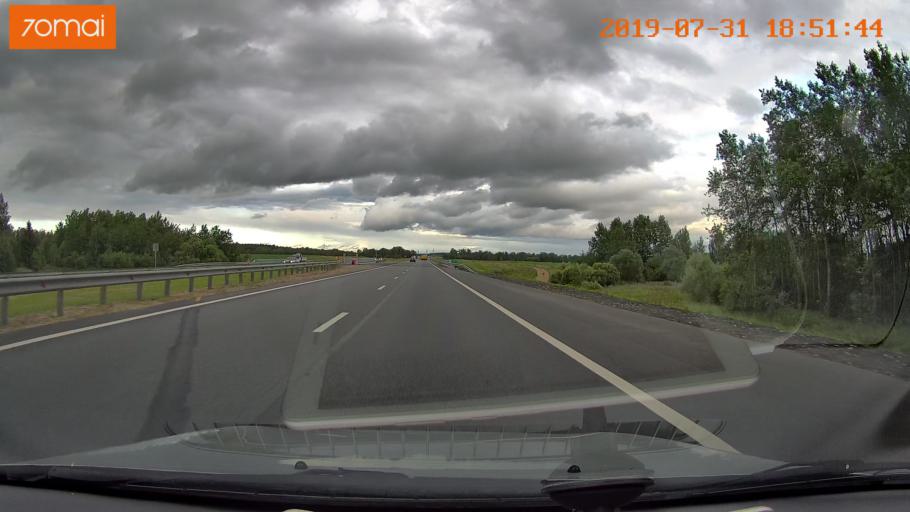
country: RU
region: Moskovskaya
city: Voskresensk
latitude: 55.2195
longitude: 38.6145
